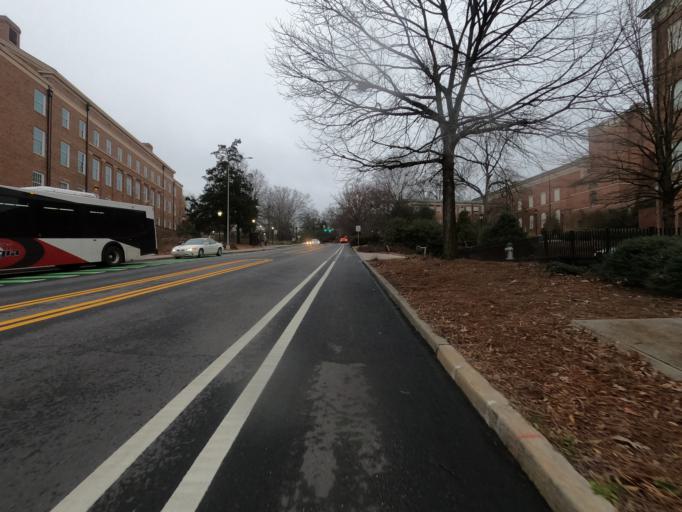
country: US
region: Georgia
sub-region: Clarke County
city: Athens
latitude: 33.9518
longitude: -83.3768
